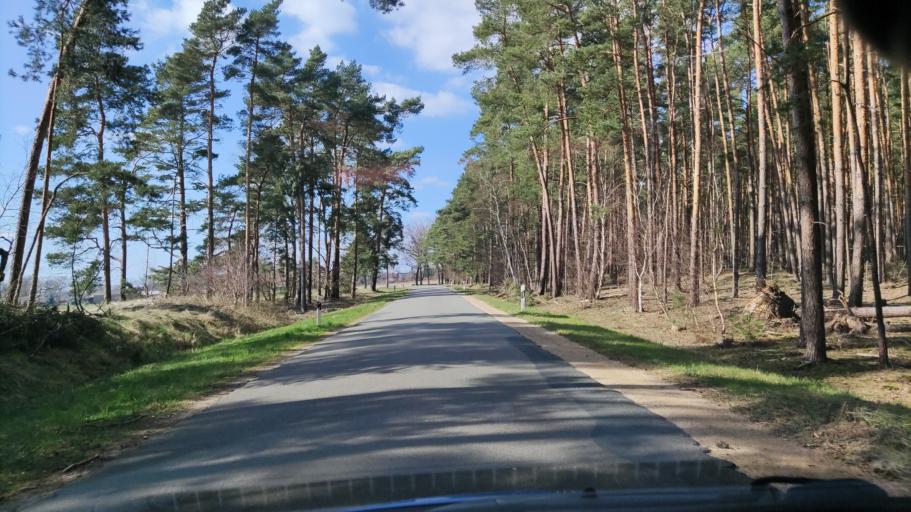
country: DE
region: Lower Saxony
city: Trebel
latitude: 53.0030
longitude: 11.2830
